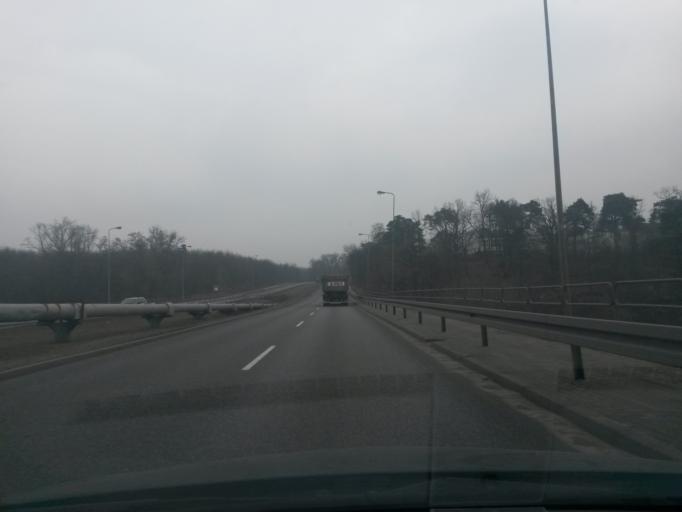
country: PL
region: Masovian Voivodeship
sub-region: Powiat legionowski
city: Nieporet
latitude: 52.4619
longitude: 21.0205
